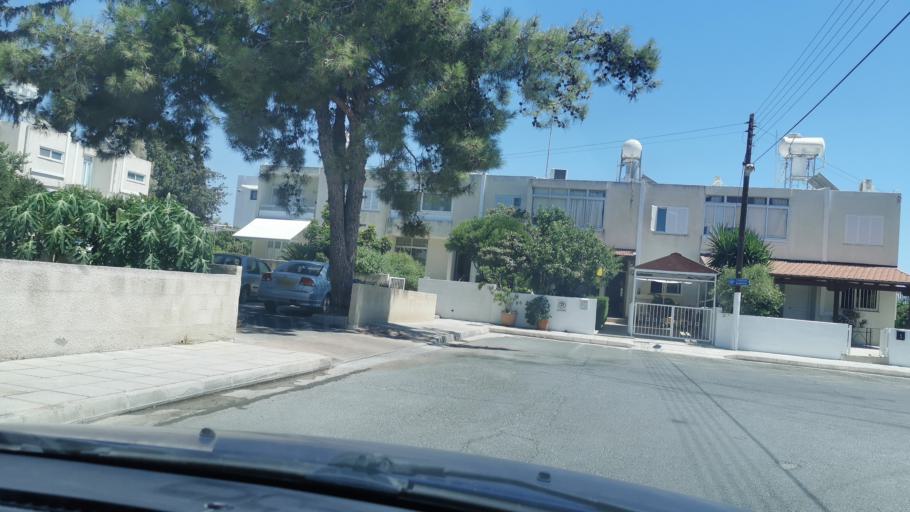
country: CY
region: Limassol
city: Limassol
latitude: 34.6973
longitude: 33.0669
